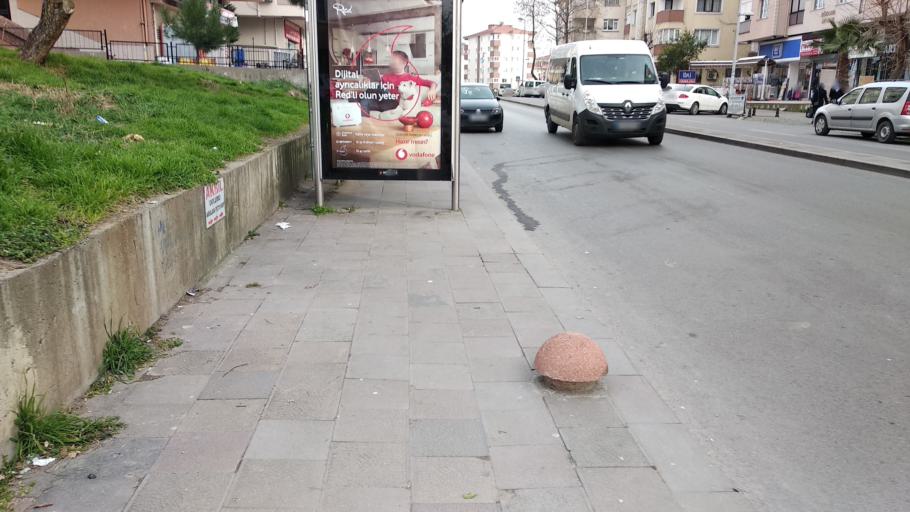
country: TR
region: Istanbul
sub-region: Atasehir
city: Atasehir
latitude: 40.9702
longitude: 29.1149
